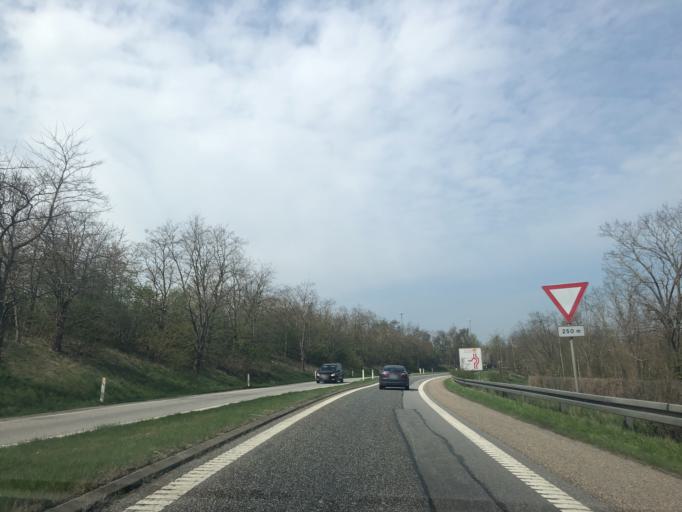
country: DK
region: Zealand
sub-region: Roskilde Kommune
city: Vindinge
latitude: 55.6373
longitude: 12.1164
